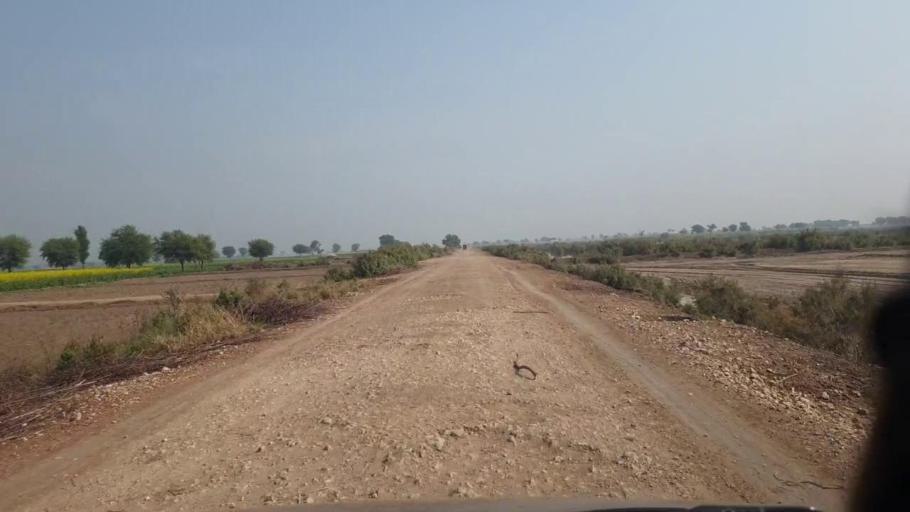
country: PK
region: Sindh
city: Shahdadpur
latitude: 26.0413
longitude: 68.4853
